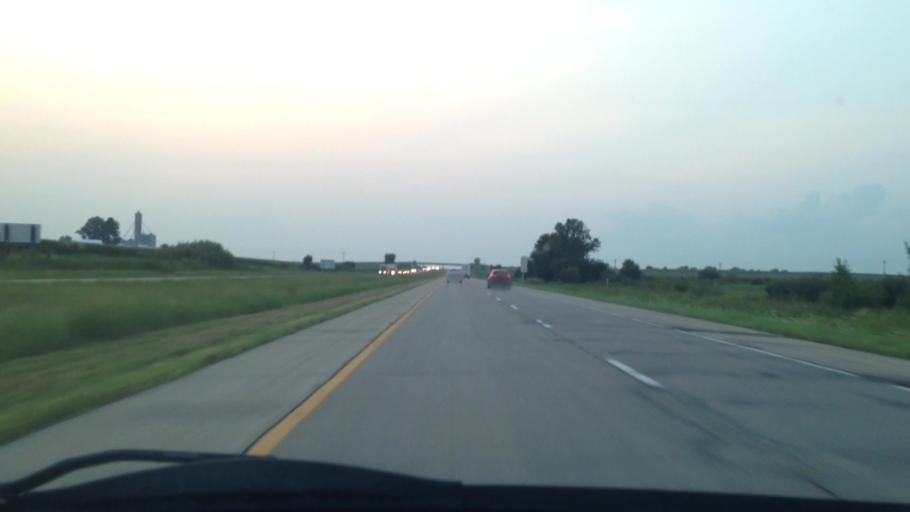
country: US
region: Iowa
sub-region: Benton County
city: Urbana
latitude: 42.2515
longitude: -91.8990
